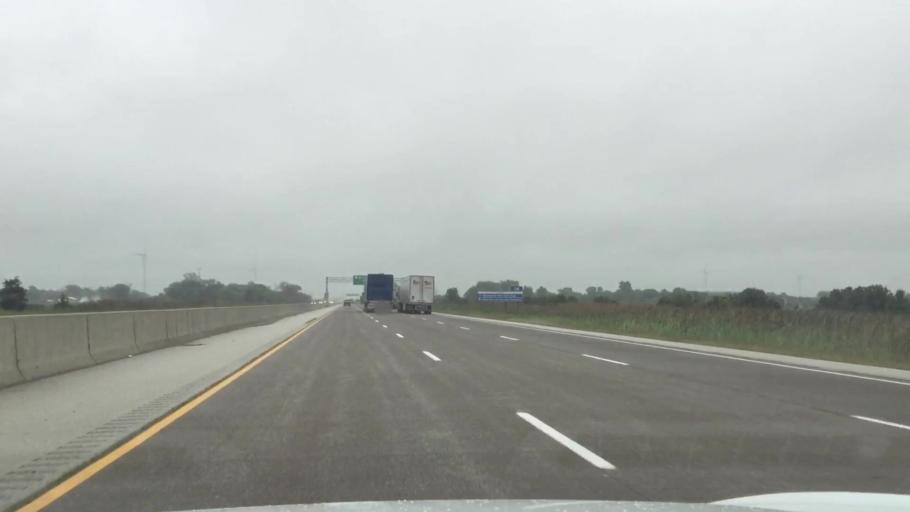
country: US
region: Michigan
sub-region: Wayne County
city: Grosse Pointe
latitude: 42.2372
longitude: -82.7287
